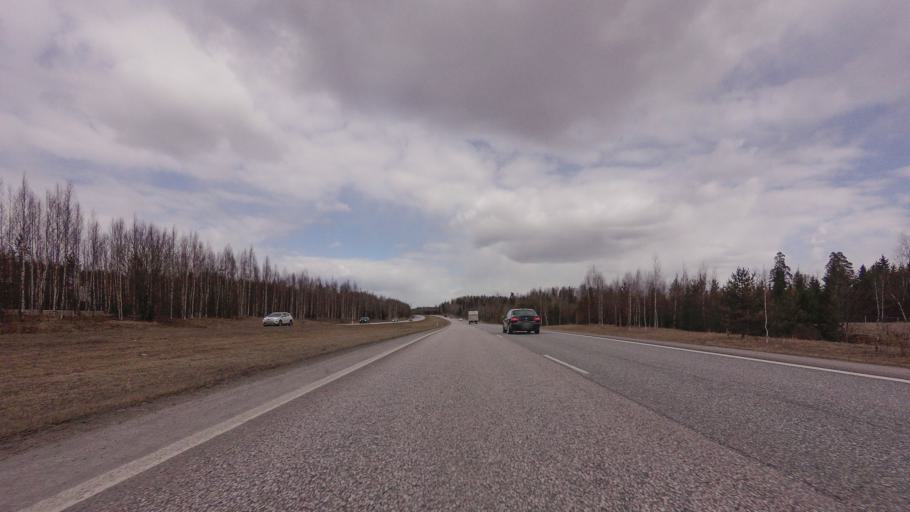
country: FI
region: Uusimaa
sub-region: Helsinki
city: Nurmijaervi
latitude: 60.4069
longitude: 24.8222
